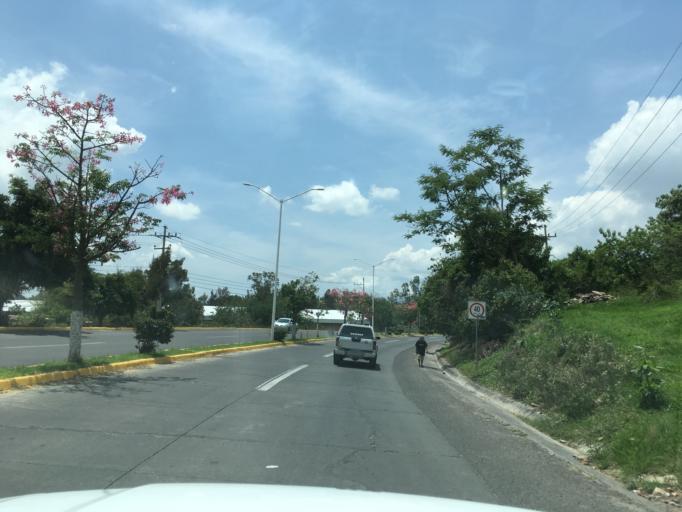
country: MX
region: Jalisco
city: Tlajomulco de Zuniga
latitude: 20.4674
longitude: -103.4507
